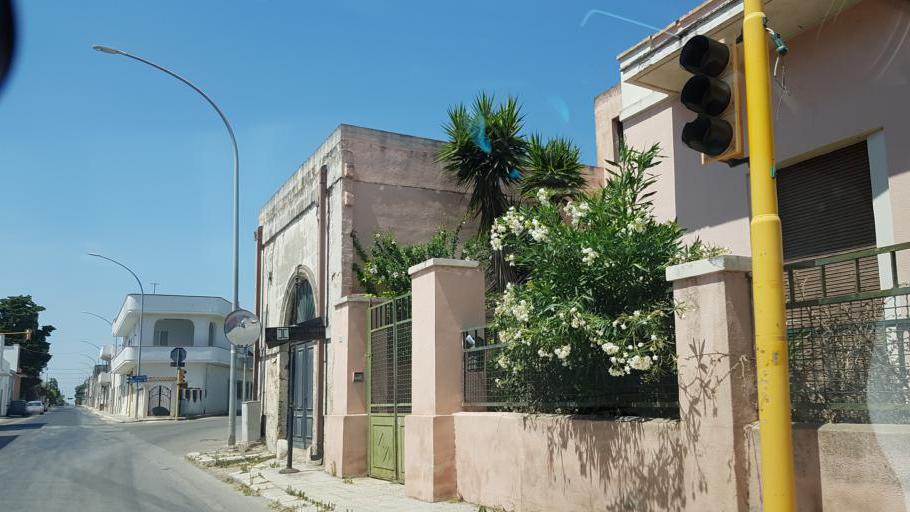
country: IT
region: Apulia
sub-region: Provincia di Brindisi
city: San Donaci
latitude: 40.4505
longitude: 17.9201
